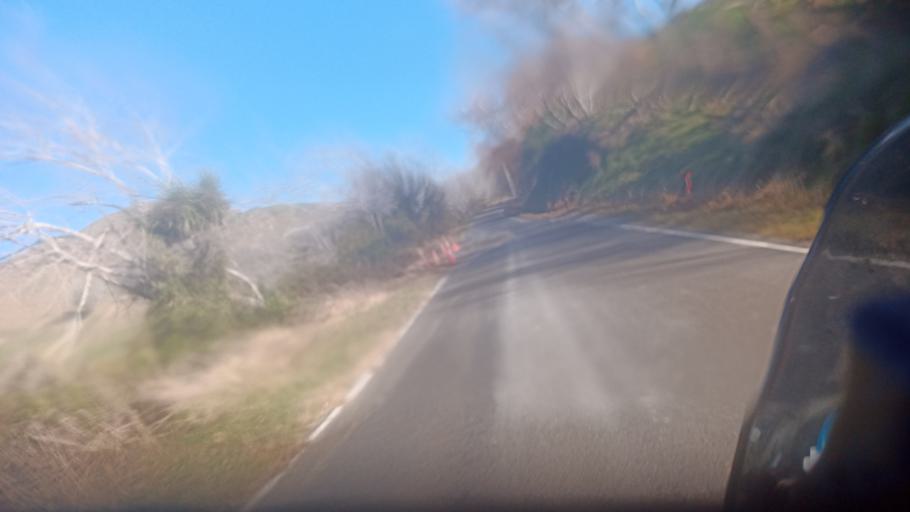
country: NZ
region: Gisborne
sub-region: Gisborne District
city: Gisborne
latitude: -38.5709
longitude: 177.5942
